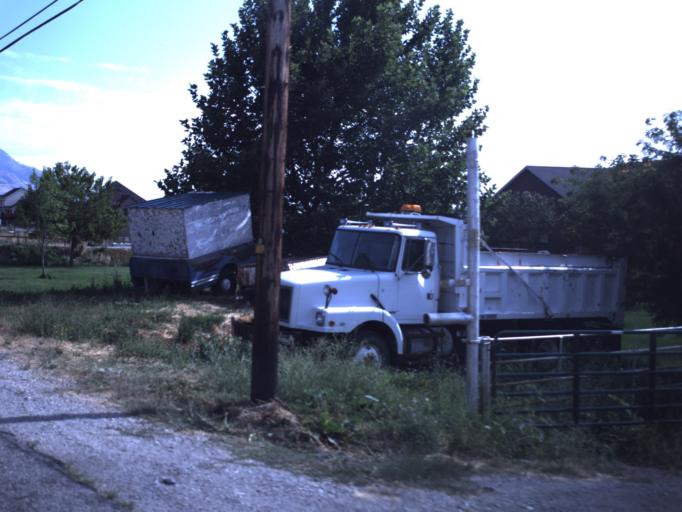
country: US
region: Utah
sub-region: Box Elder County
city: Brigham City
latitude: 41.5756
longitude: -112.0319
